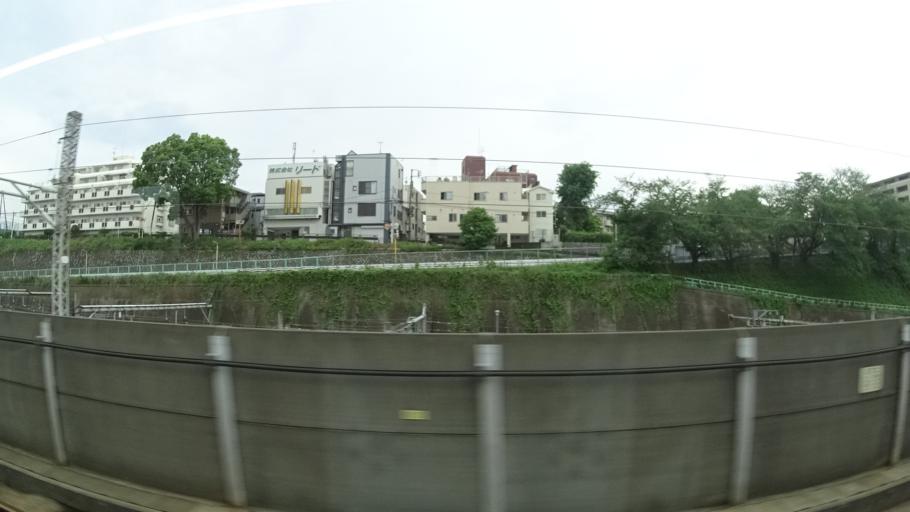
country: JP
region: Tokyo
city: Tokyo
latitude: 35.7352
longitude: 139.7648
